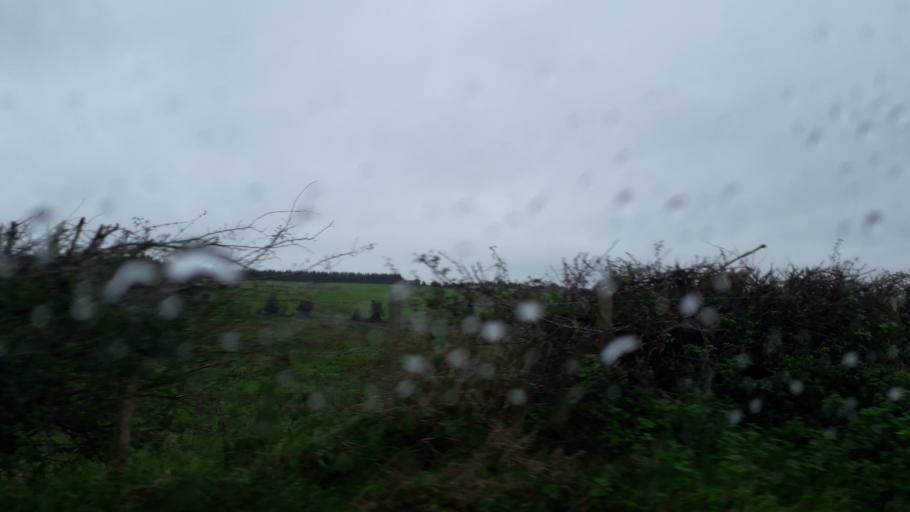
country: IE
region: Connaught
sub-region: Roscommon
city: Boyle
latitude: 53.7920
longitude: -8.2795
